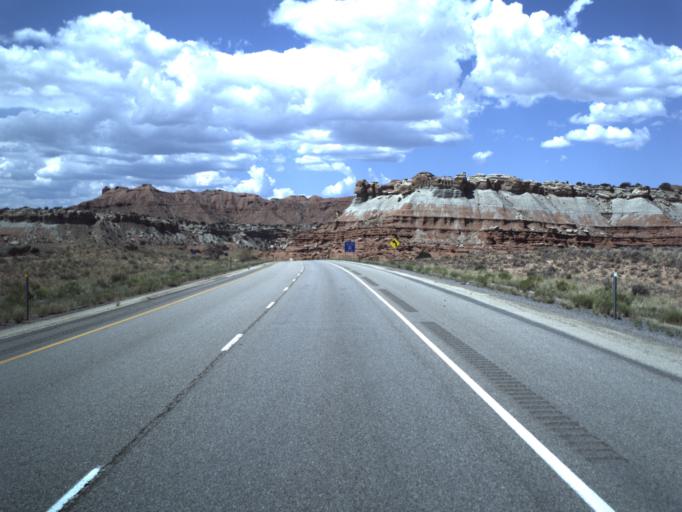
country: US
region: Utah
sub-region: Emery County
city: Ferron
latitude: 38.8402
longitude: -111.0948
